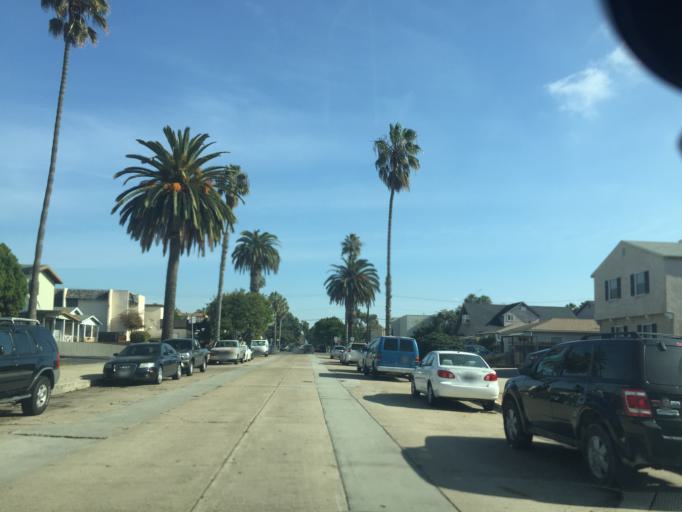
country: US
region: California
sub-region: San Diego County
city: La Jolla
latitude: 32.7942
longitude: -117.2522
